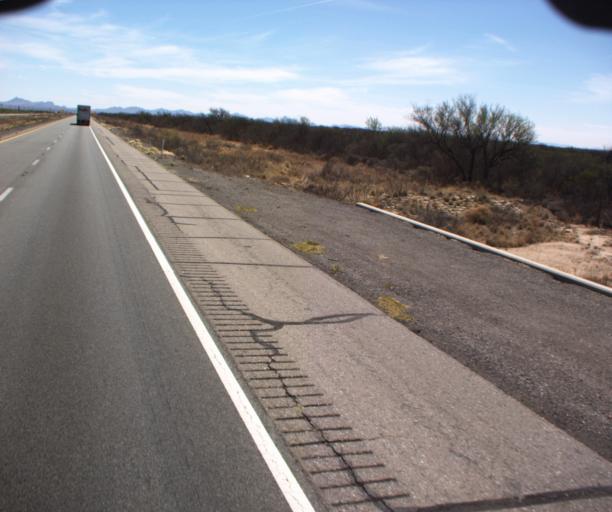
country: US
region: Arizona
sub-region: Cochise County
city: Willcox
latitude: 32.2893
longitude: -109.3196
